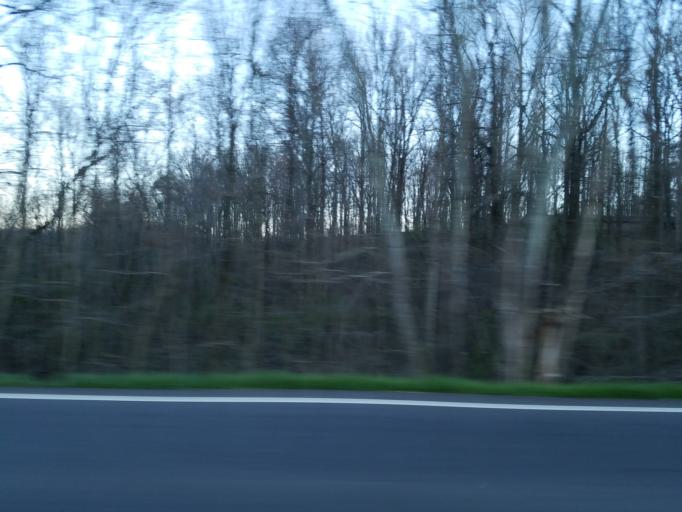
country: US
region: Georgia
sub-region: Forsyth County
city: Cumming
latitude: 34.2896
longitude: -84.0253
